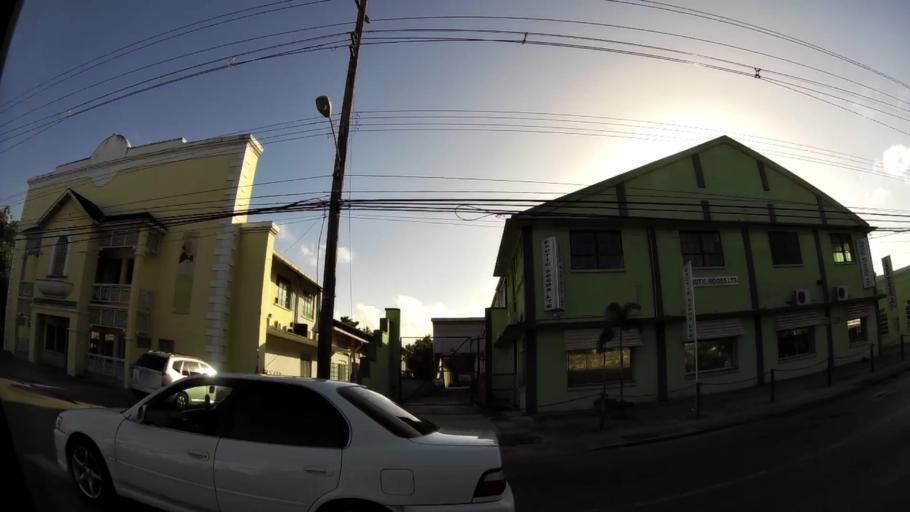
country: BB
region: Saint Michael
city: Bridgetown
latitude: 13.0825
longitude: -59.6078
